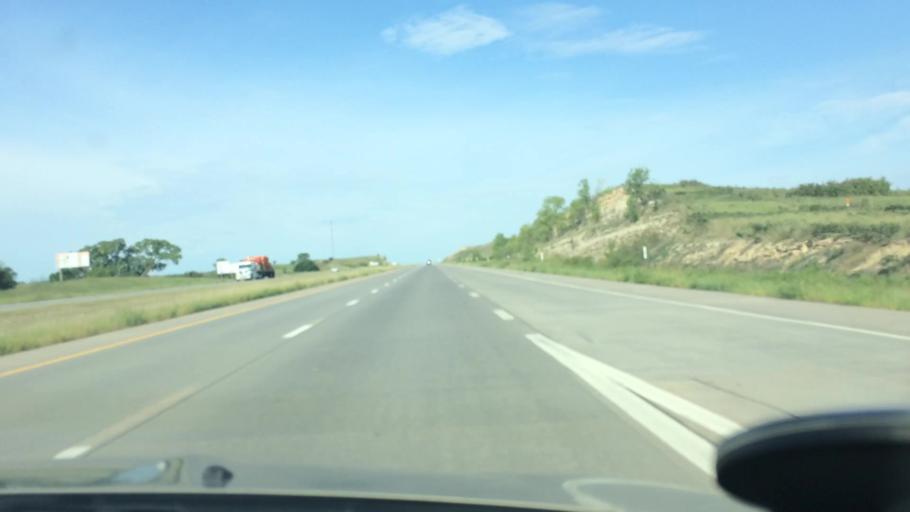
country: US
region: Kansas
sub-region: Riley County
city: Ogden
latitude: 39.0657
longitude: -96.6599
